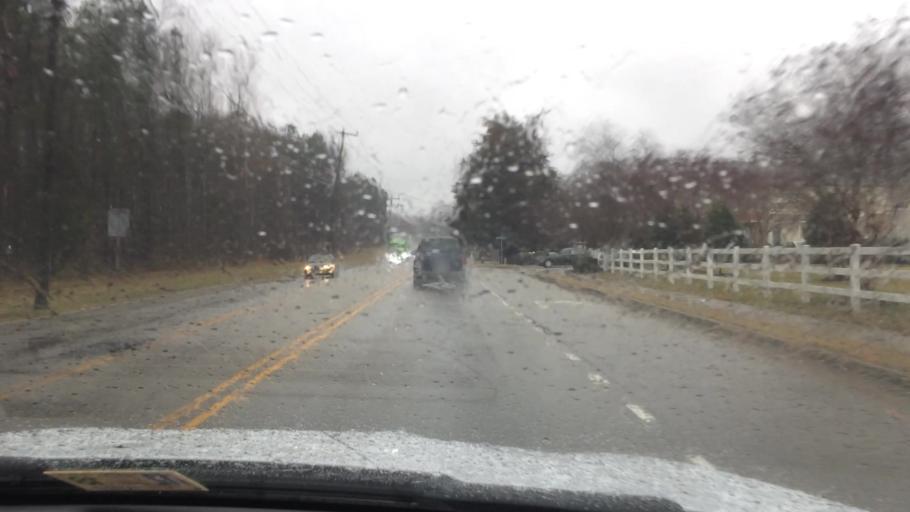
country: US
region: Virginia
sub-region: City of Williamsburg
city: Williamsburg
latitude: 37.2122
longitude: -76.6183
